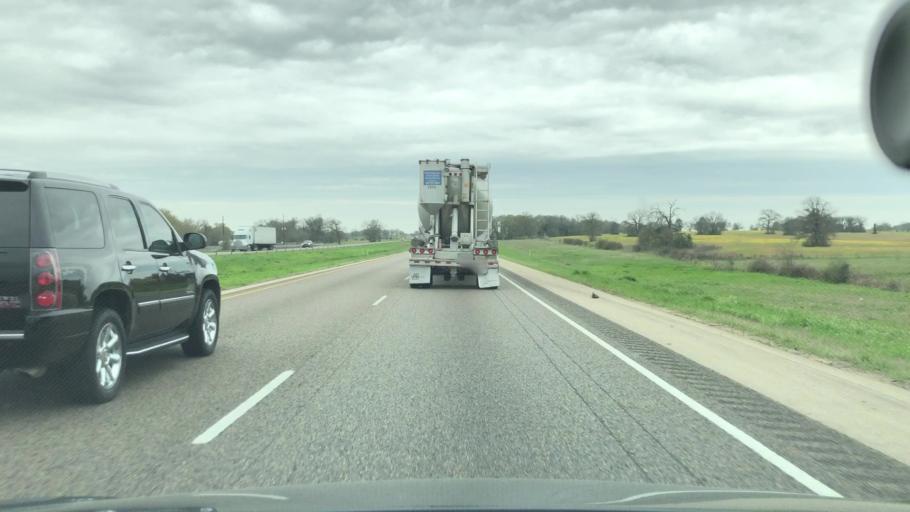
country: US
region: Texas
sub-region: Madison County
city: Madisonville
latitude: 31.0600
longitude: -95.9500
